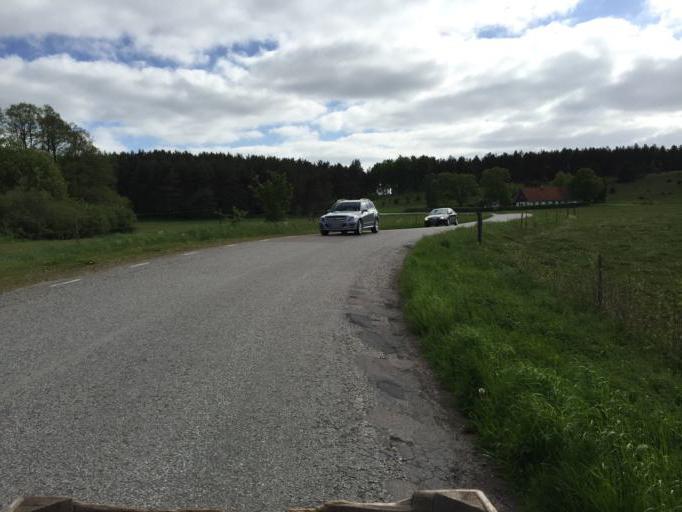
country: SE
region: Skane
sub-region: Sjobo Kommun
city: Blentarp
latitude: 55.6621
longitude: 13.6171
